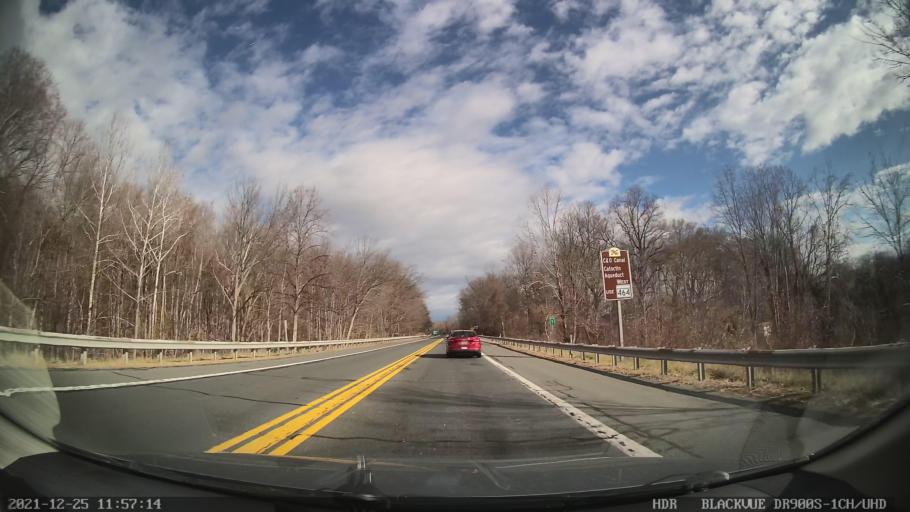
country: US
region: Maryland
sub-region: Frederick County
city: Point of Rocks
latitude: 39.2820
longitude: -77.5365
